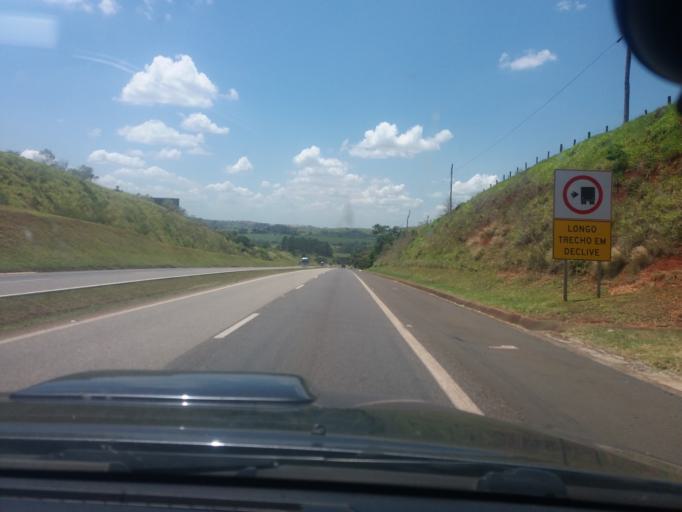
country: BR
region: Sao Paulo
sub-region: Tatui
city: Tatui
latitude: -23.3985
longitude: -47.9260
